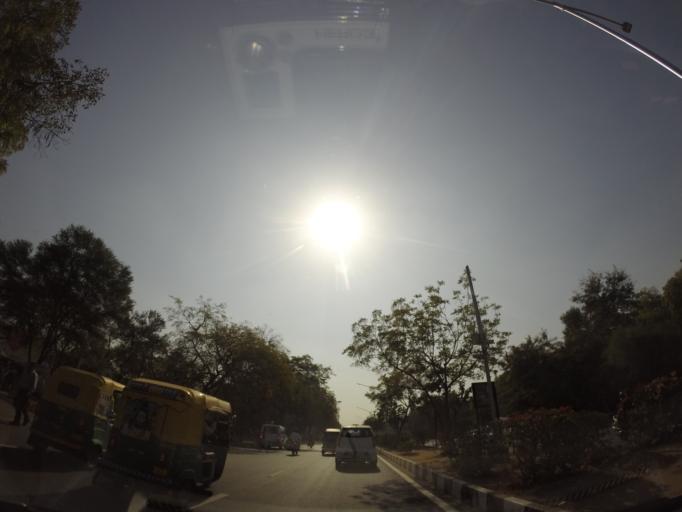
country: IN
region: Gujarat
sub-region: Gandhinagar
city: Ghandinagar
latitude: 23.2177
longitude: 72.6418
